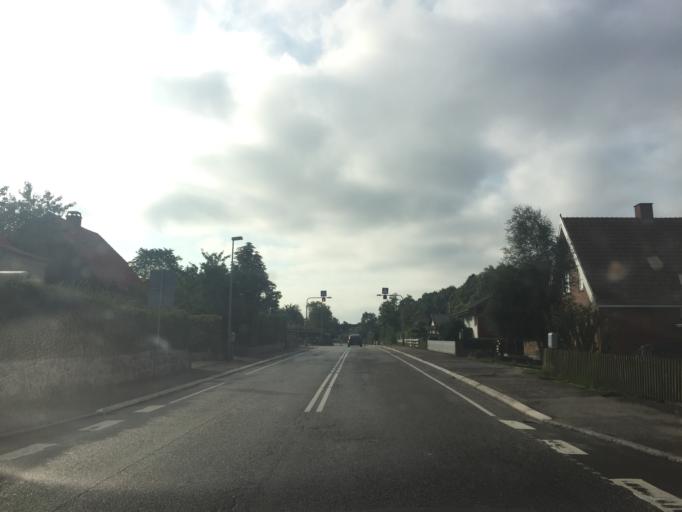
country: DK
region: Capital Region
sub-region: Halsnaes Kommune
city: Frederiksvaerk
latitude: 55.9539
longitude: 12.0251
